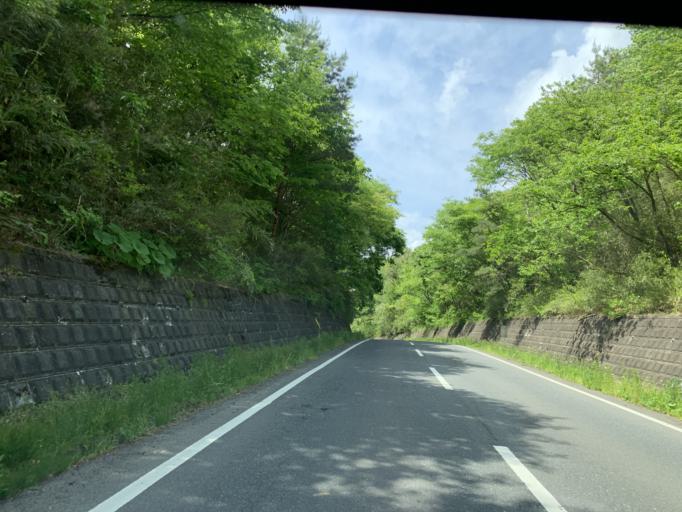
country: JP
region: Iwate
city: Ichinoseki
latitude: 38.7845
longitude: 141.0009
